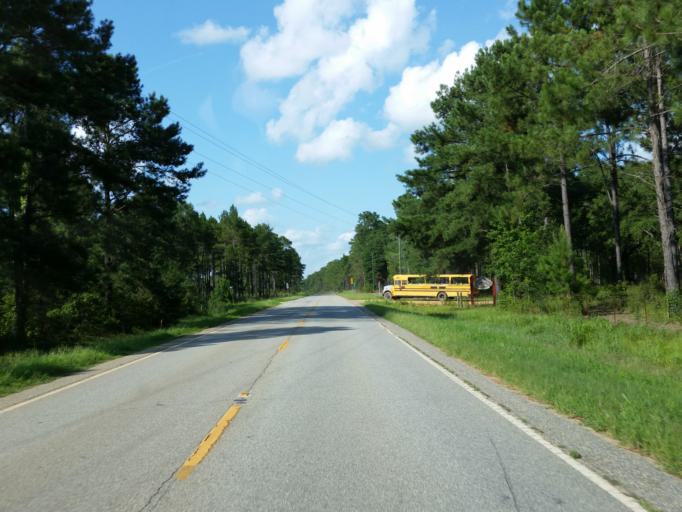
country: US
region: Georgia
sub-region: Lee County
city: Leesburg
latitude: 31.8547
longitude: -84.0807
